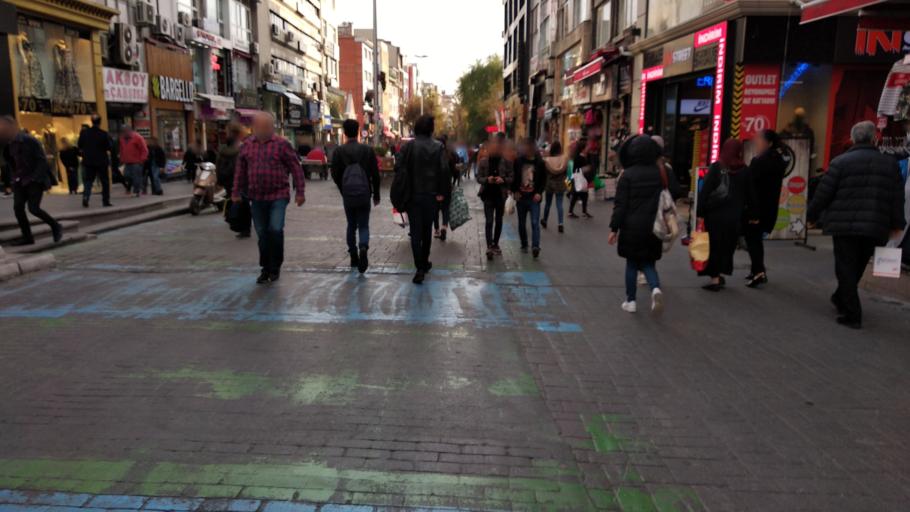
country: TR
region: Istanbul
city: Bahcelievler
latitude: 40.9782
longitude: 28.8745
